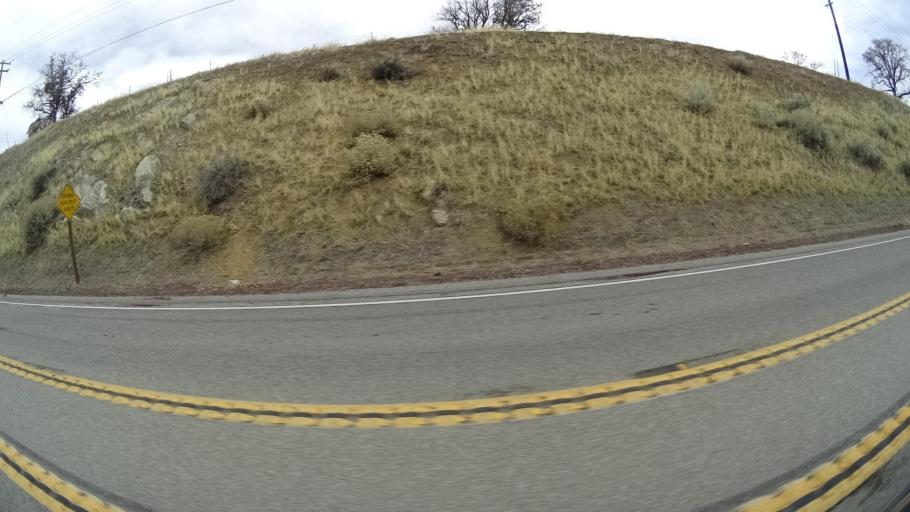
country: US
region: California
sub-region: Kern County
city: Golden Hills
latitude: 35.1132
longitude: -118.5237
